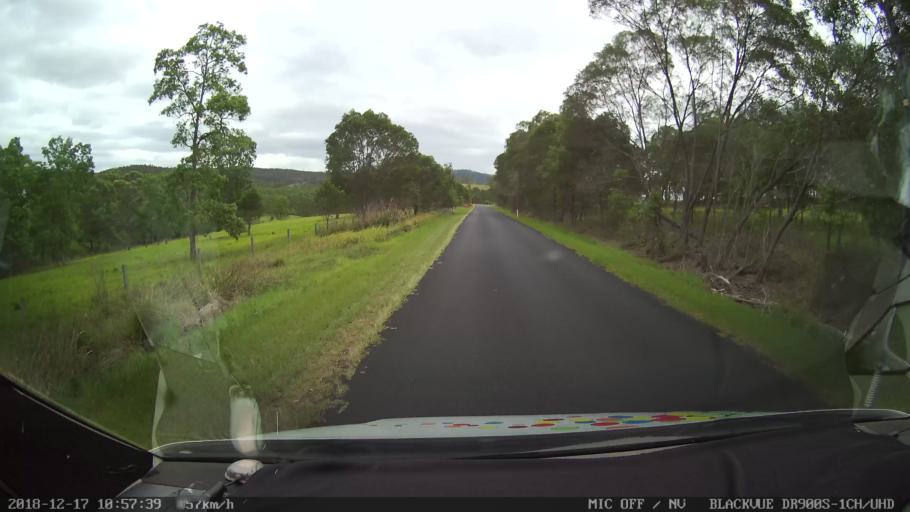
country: AU
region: New South Wales
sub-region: Richmond Valley
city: Casino
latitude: -28.8240
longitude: 152.5986
